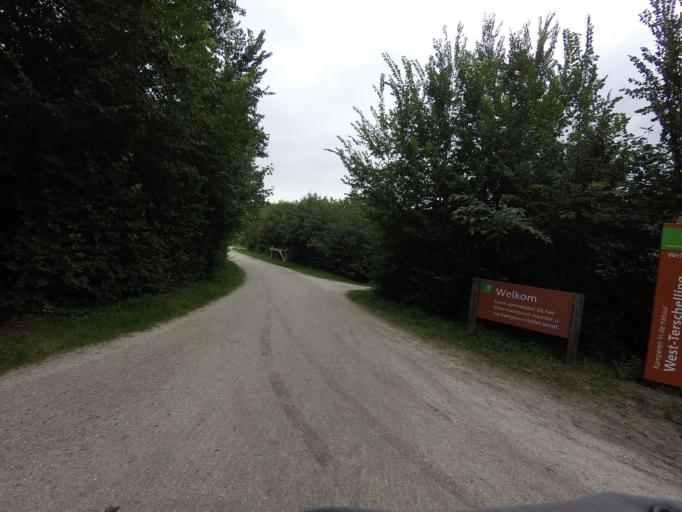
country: NL
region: Friesland
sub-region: Gemeente Terschelling
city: West-Terschelling
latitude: 53.3702
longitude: 5.2155
